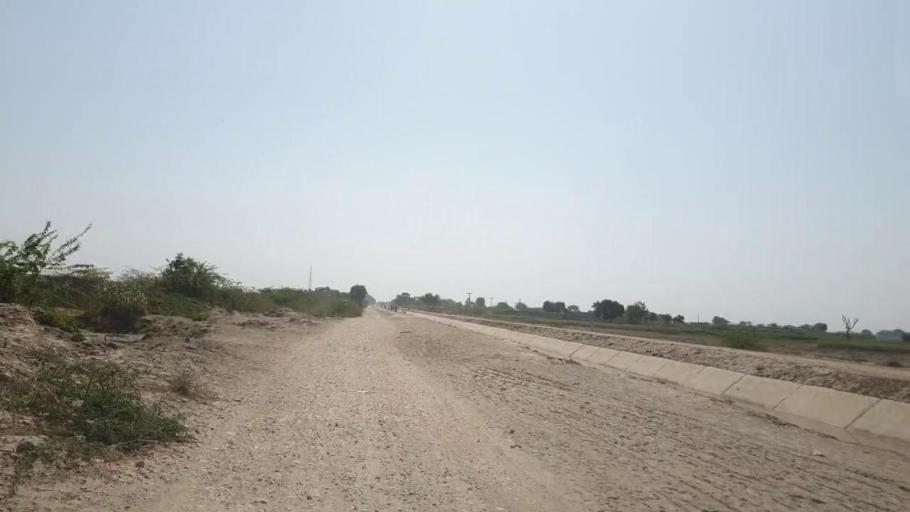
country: PK
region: Sindh
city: Naukot
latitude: 24.9832
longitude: 69.4751
